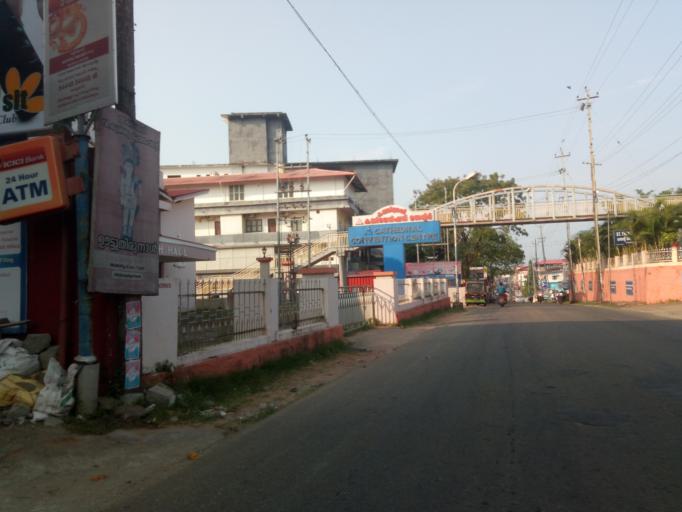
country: IN
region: Kerala
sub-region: Thrissur District
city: Irinjalakuda
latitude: 10.3438
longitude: 76.2165
